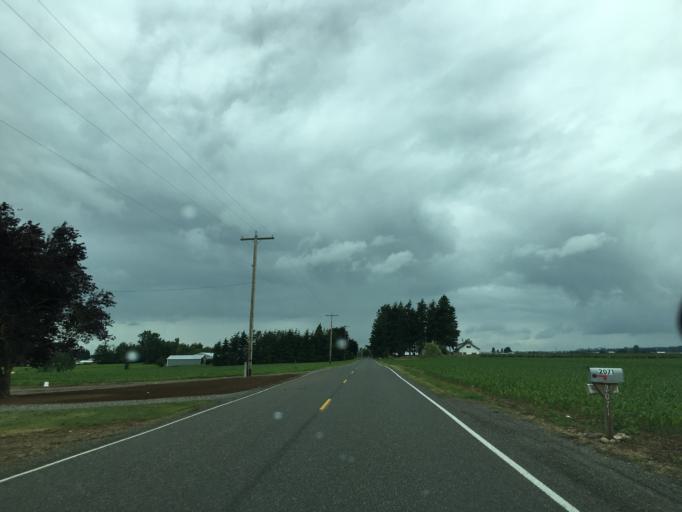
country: US
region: Washington
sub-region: Whatcom County
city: Everson
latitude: 48.9821
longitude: -122.3756
